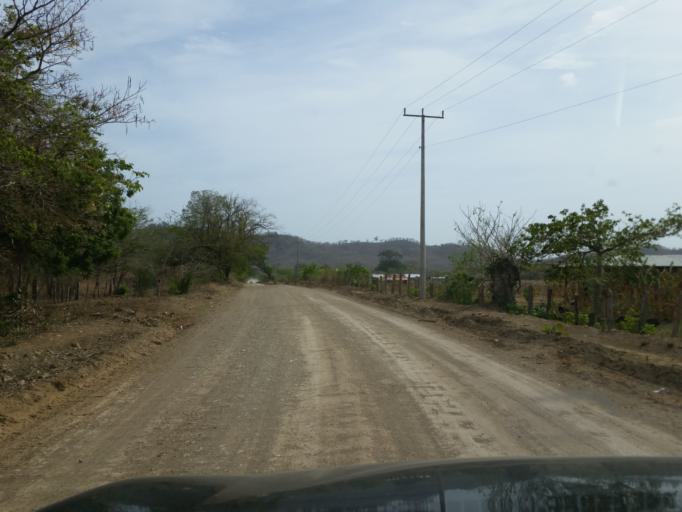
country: NI
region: Rivas
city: Tola
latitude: 11.4536
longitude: -86.0524
